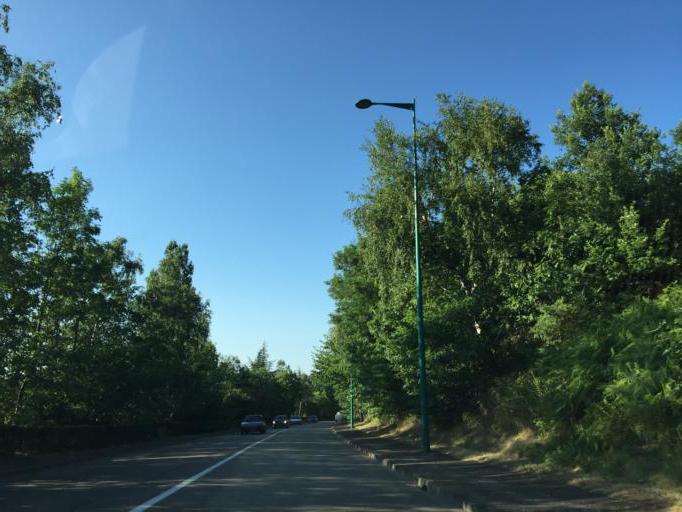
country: FR
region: Rhone-Alpes
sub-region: Departement de la Loire
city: La Talaudiere
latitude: 45.4632
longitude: 4.4277
